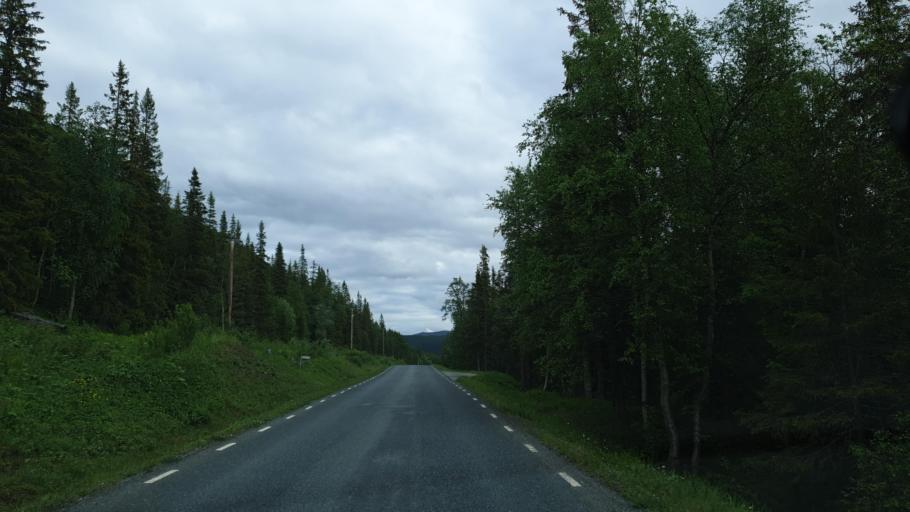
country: SE
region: Vaesterbotten
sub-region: Vilhelmina Kommun
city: Sjoberg
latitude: 65.2431
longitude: 15.4344
